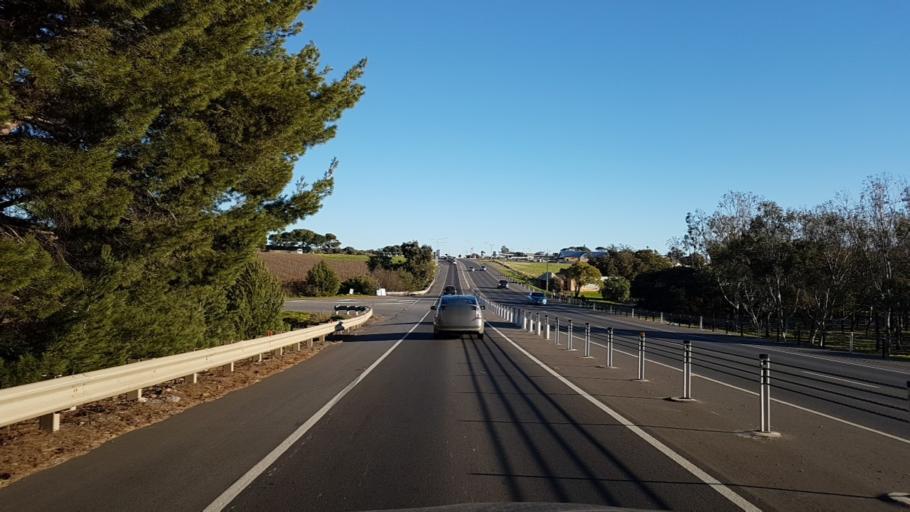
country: AU
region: South Australia
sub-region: Onkaparinga
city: Aldinga
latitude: -35.2637
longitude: 138.4880
